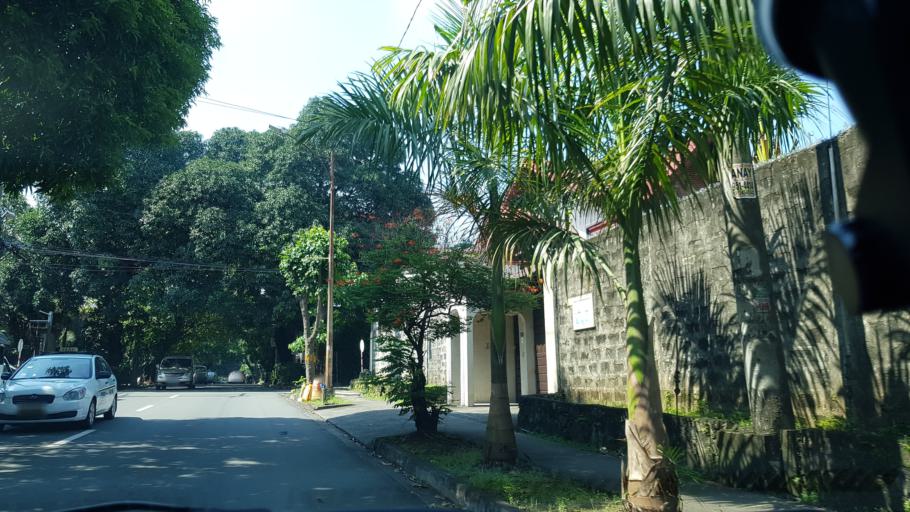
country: PH
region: Metro Manila
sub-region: San Juan
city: San Juan
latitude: 14.6201
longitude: 121.0280
